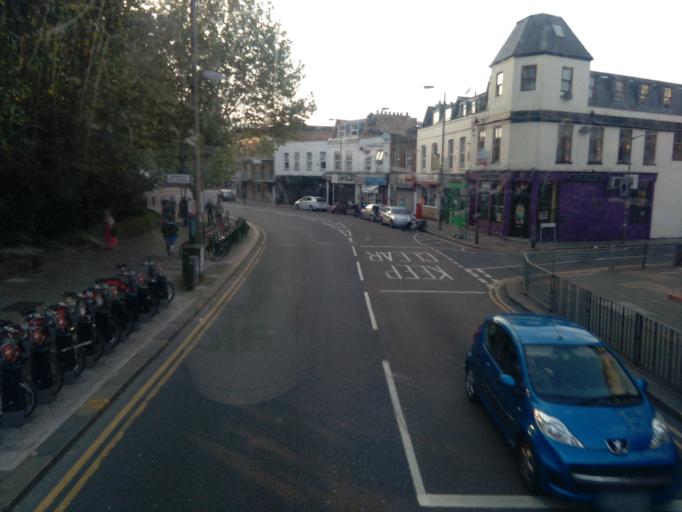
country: GB
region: England
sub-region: Greater London
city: Battersea
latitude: 51.4665
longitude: -0.1696
